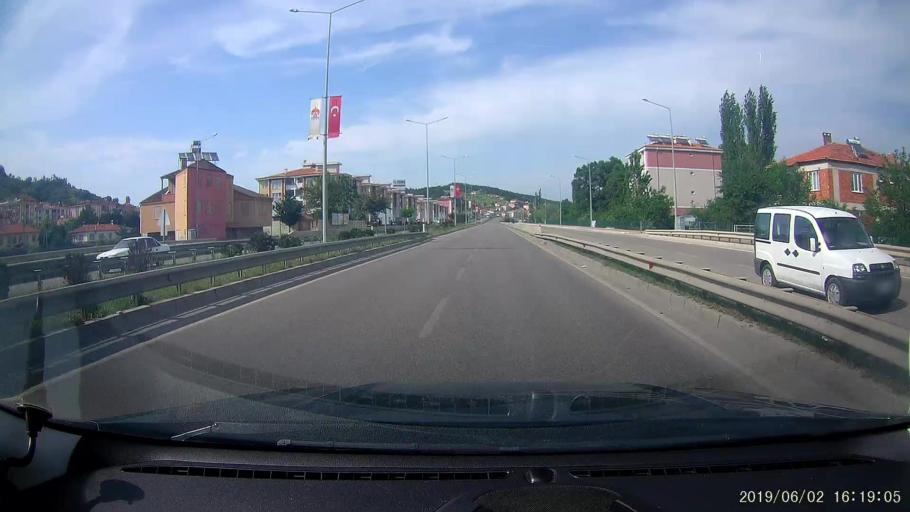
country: TR
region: Samsun
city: Havza
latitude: 40.9631
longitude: 35.6670
